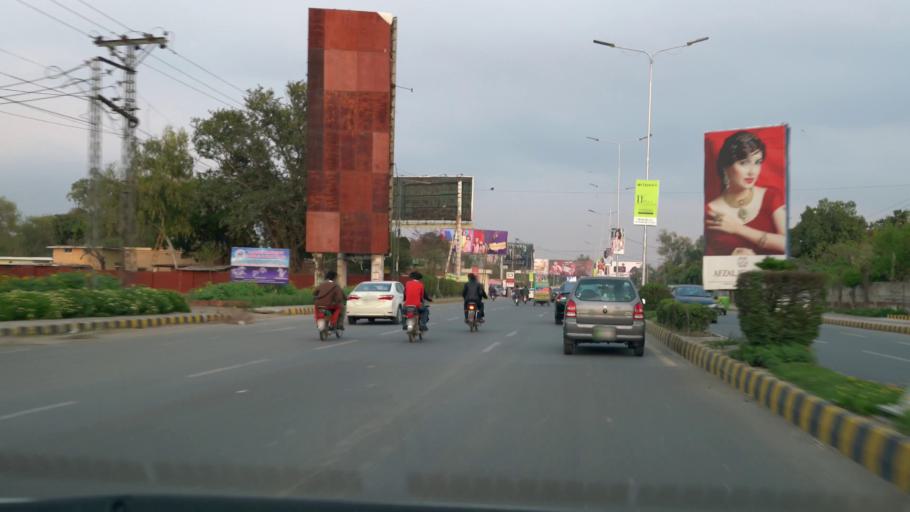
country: PK
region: Punjab
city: Lahore
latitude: 31.5017
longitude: 74.3646
